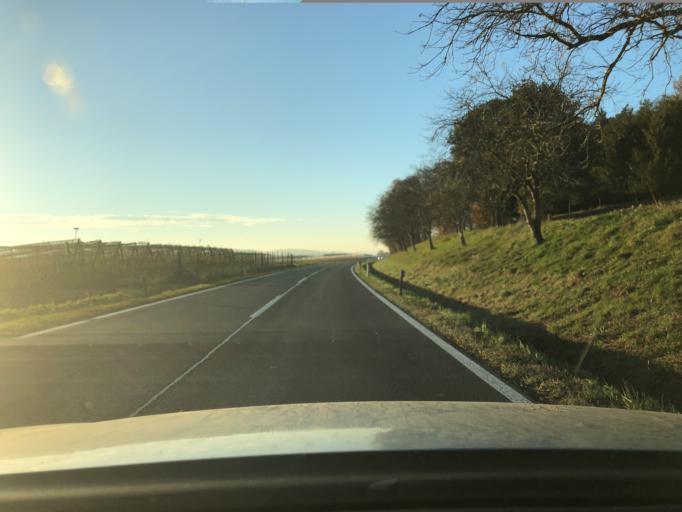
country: AT
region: Styria
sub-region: Politischer Bezirk Hartberg-Fuerstenfeld
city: Ilz
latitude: 47.0891
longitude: 15.8949
